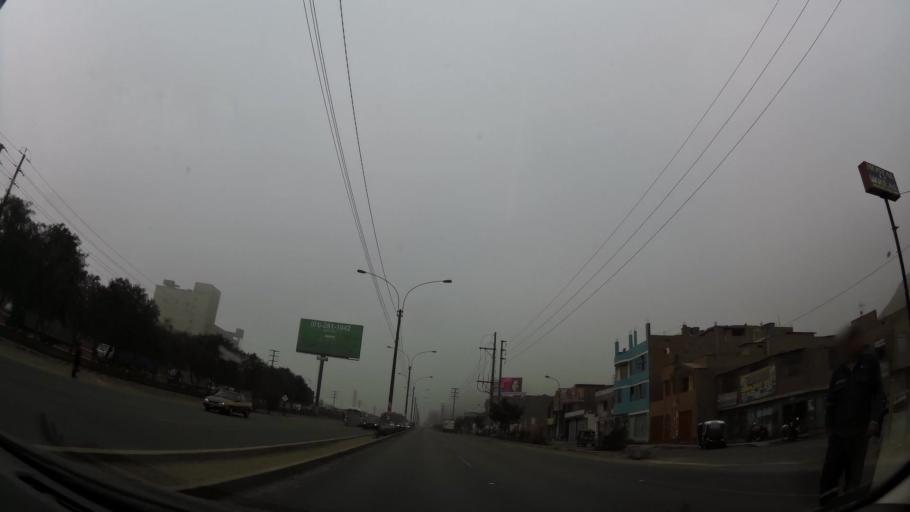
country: PE
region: Lima
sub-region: Lima
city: Chaclacayo
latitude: -11.9922
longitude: -76.8249
